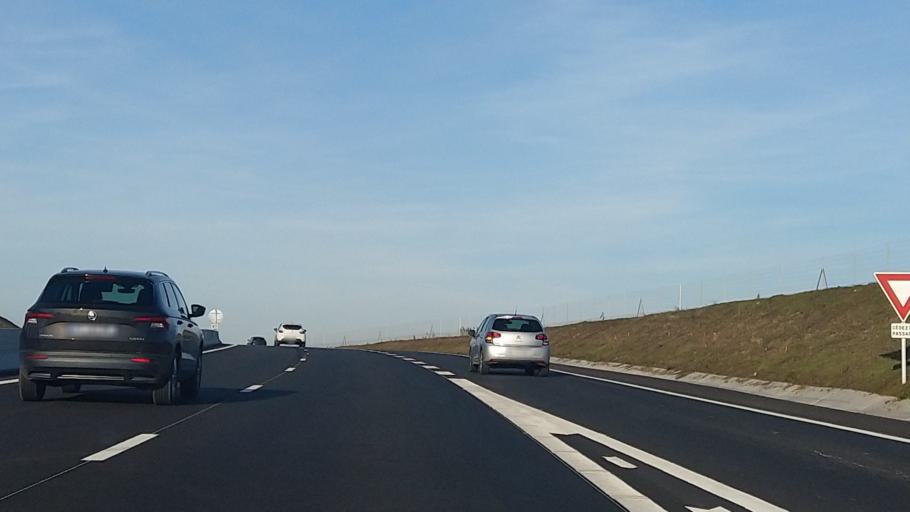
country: FR
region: Ile-de-France
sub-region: Departement du Val-d'Oise
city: Montsoult
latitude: 49.0724
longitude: 2.3328
